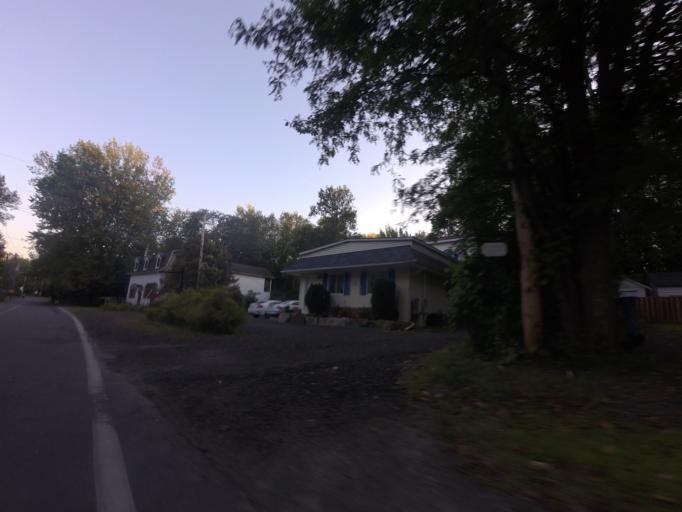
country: CA
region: Quebec
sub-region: Laurentides
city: Oka
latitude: 45.4491
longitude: -74.1099
